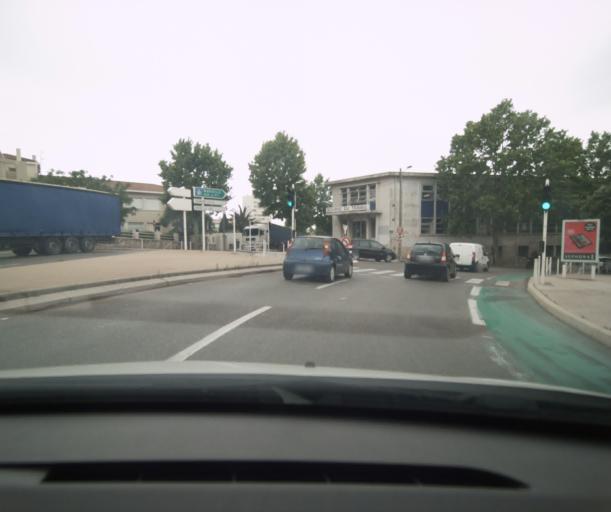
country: FR
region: Provence-Alpes-Cote d'Azur
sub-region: Departement du Var
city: Toulon
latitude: 43.1295
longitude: 5.9264
